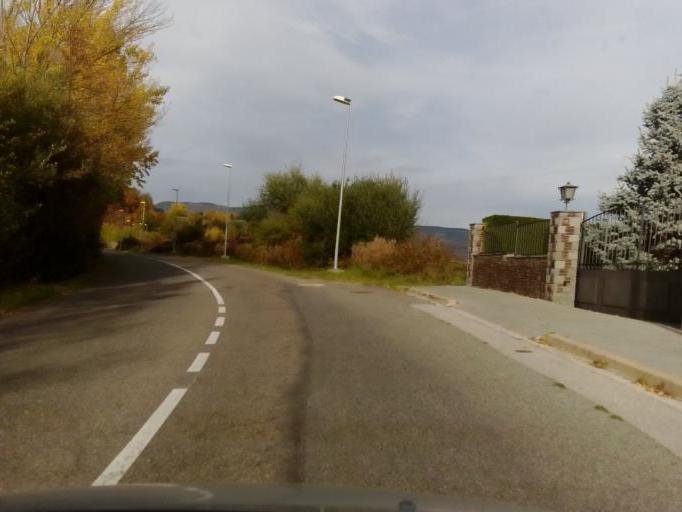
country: ES
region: Catalonia
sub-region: Provincia de Girona
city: Puigcerda
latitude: 42.4351
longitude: 1.9342
